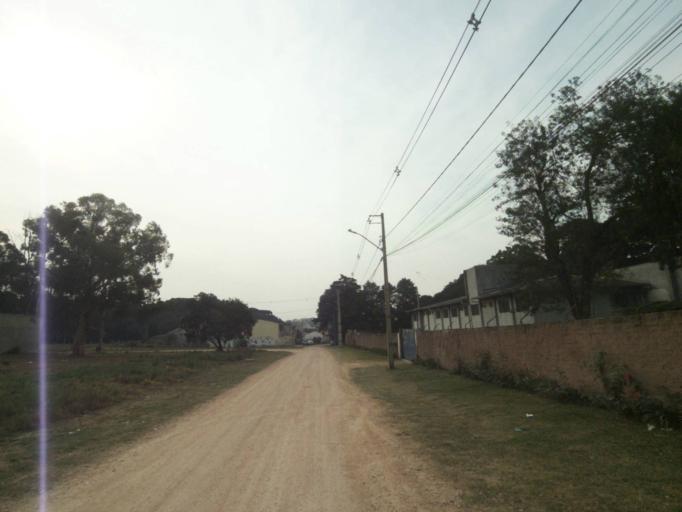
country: BR
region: Parana
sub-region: Sao Jose Dos Pinhais
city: Sao Jose dos Pinhais
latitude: -25.5262
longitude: -49.2761
